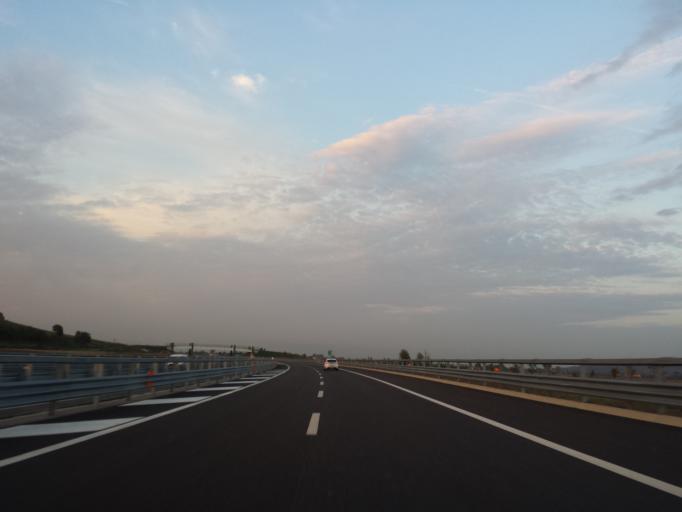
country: IT
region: Veneto
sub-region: Provincia di Vicenza
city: Albettone
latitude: 45.3603
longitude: 11.6058
